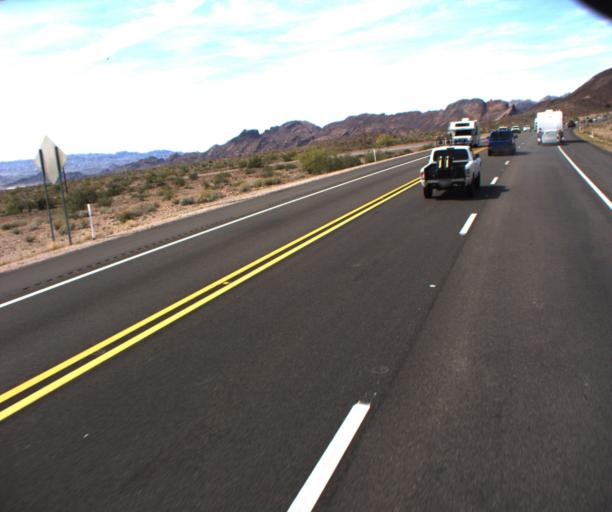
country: US
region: Arizona
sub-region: Mohave County
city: Desert Hills
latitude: 34.5850
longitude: -114.3689
